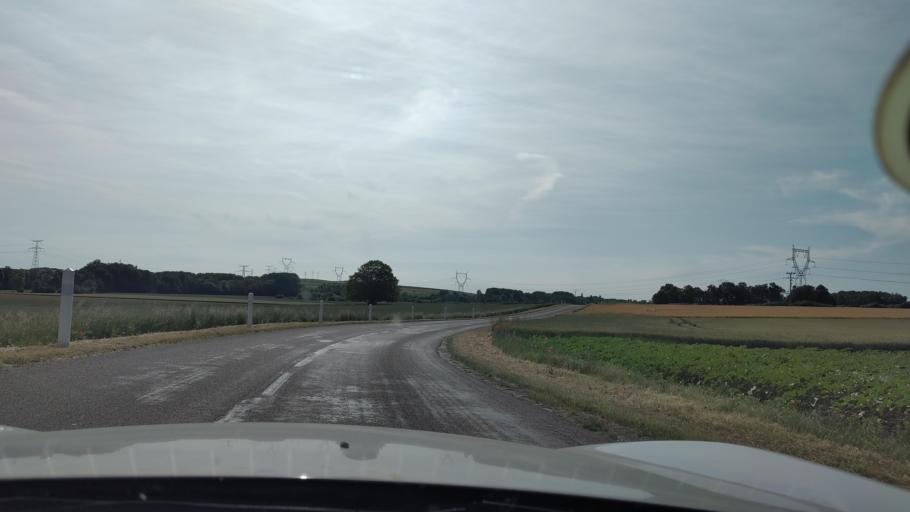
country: FR
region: Champagne-Ardenne
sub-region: Departement de l'Aube
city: Nogent-sur-Seine
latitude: 48.4616
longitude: 3.5904
